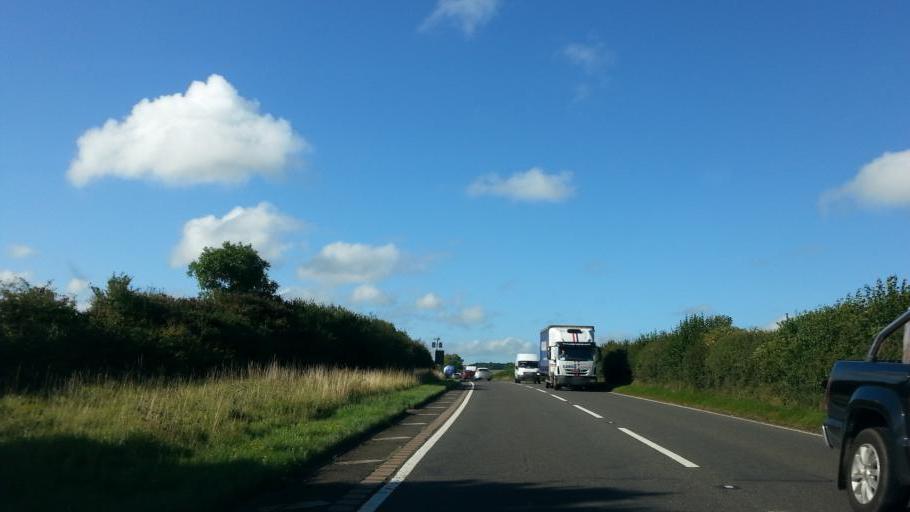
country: GB
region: England
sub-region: District of Rutland
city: Ketton
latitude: 52.5778
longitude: -0.5656
